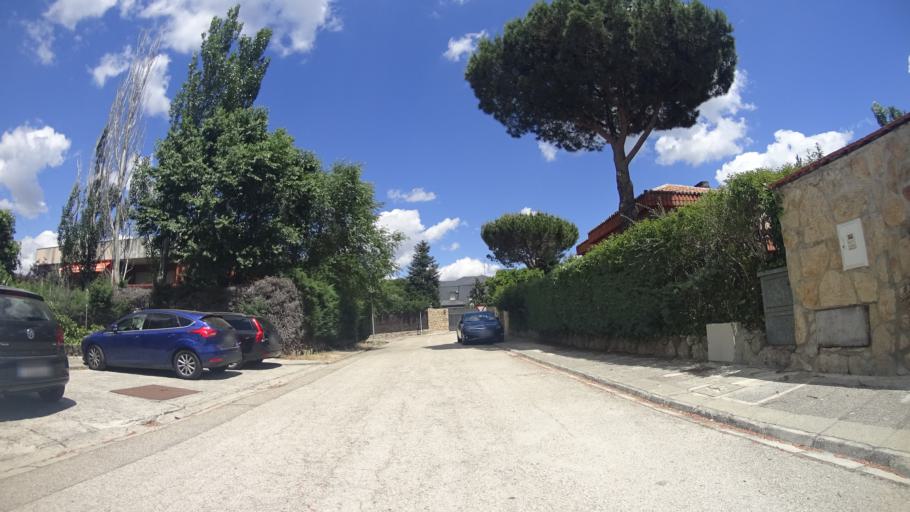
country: ES
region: Madrid
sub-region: Provincia de Madrid
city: Hoyo de Manzanares
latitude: 40.6116
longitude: -3.9321
